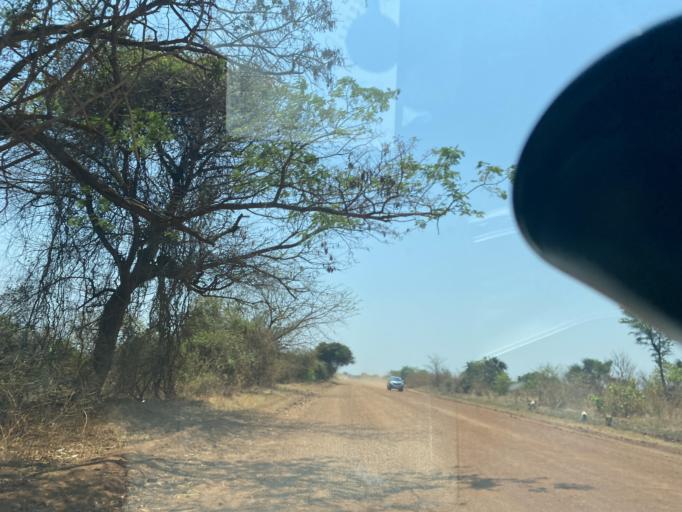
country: ZM
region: Southern
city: Nakambala
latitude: -15.4707
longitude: 27.9024
